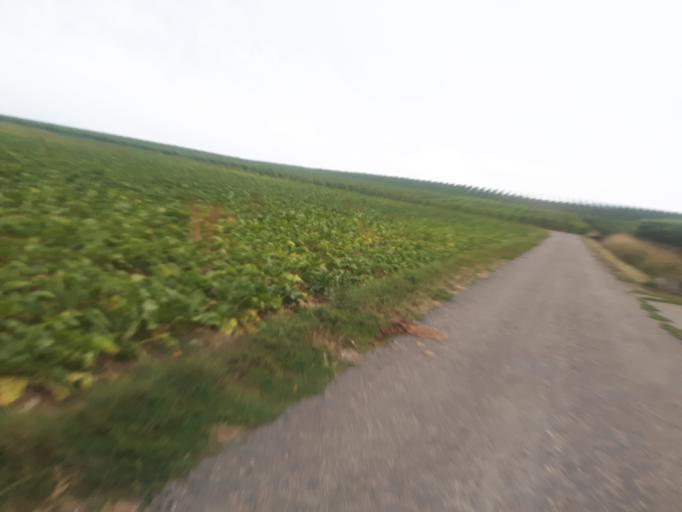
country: DE
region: Baden-Wuerttemberg
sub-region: Regierungsbezirk Stuttgart
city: Leingarten
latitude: 49.1353
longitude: 9.0939
